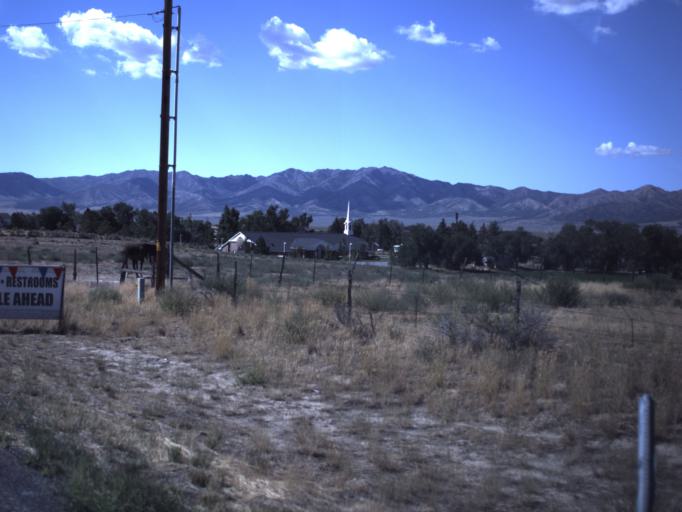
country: US
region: Utah
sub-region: Tooele County
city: Tooele
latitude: 40.0975
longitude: -112.4309
